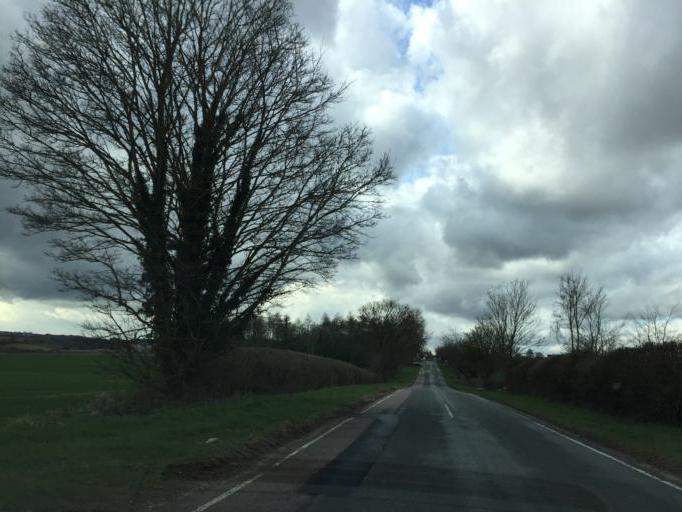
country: GB
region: England
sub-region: Oxfordshire
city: Stonesfield
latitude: 51.8546
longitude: -1.4203
